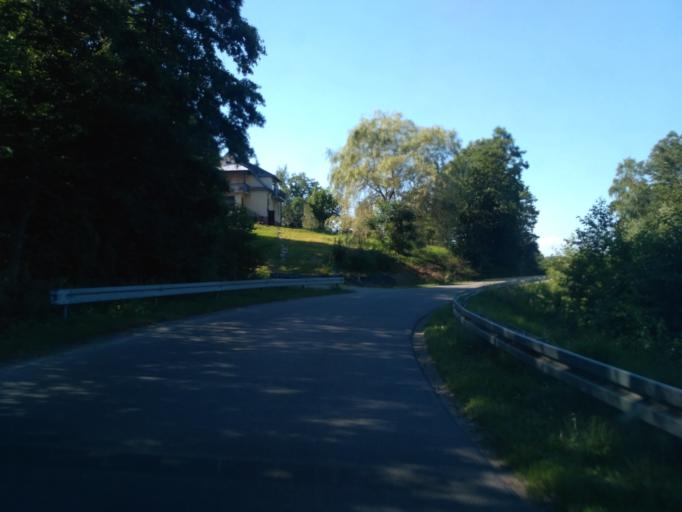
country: PL
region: Subcarpathian Voivodeship
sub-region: Powiat strzyzowski
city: Wysoka Strzyzowska
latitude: 49.7933
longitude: 21.7553
